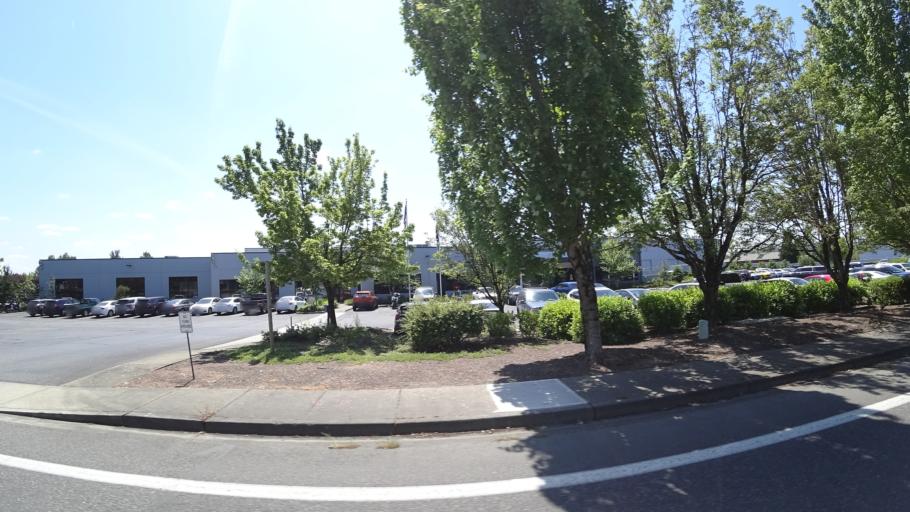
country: US
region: Oregon
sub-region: Multnomah County
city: Fairview
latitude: 45.5594
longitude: -122.5084
